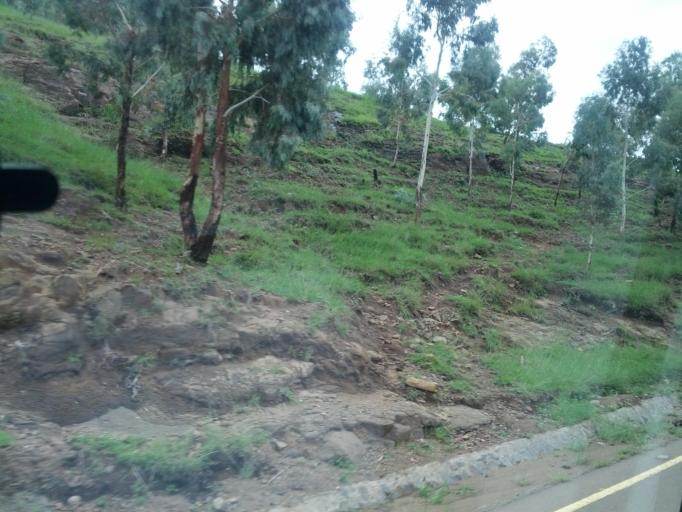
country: LS
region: Butha-Buthe
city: Butha-Buthe
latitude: -29.0373
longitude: 28.3022
